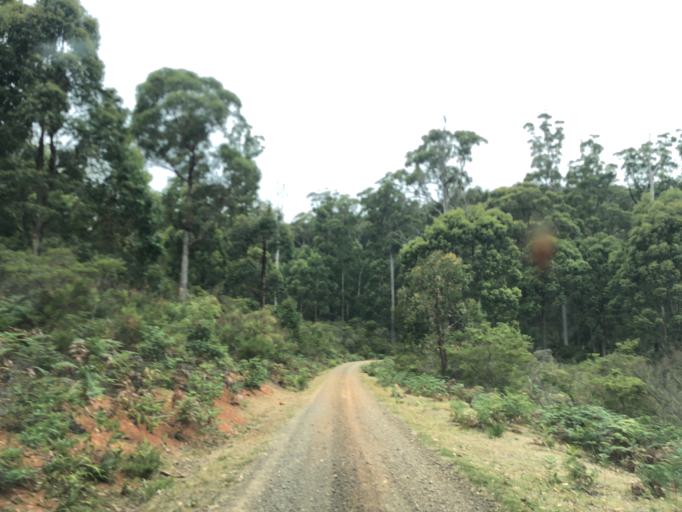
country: AU
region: Victoria
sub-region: Moorabool
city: Bacchus Marsh
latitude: -37.4376
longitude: 144.2401
